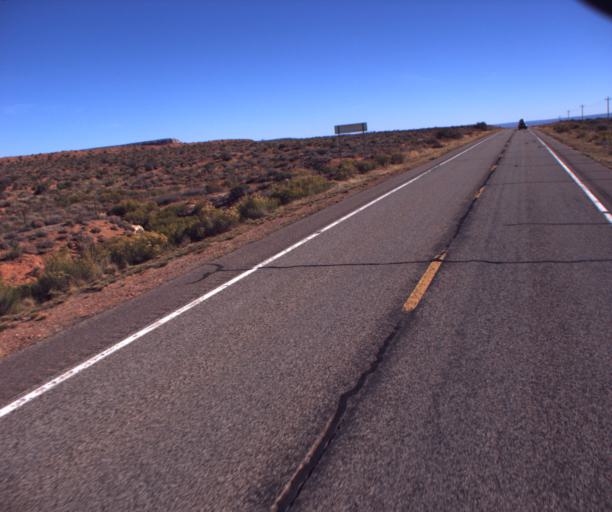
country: US
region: Arizona
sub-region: Coconino County
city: Fredonia
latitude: 36.8710
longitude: -112.6799
